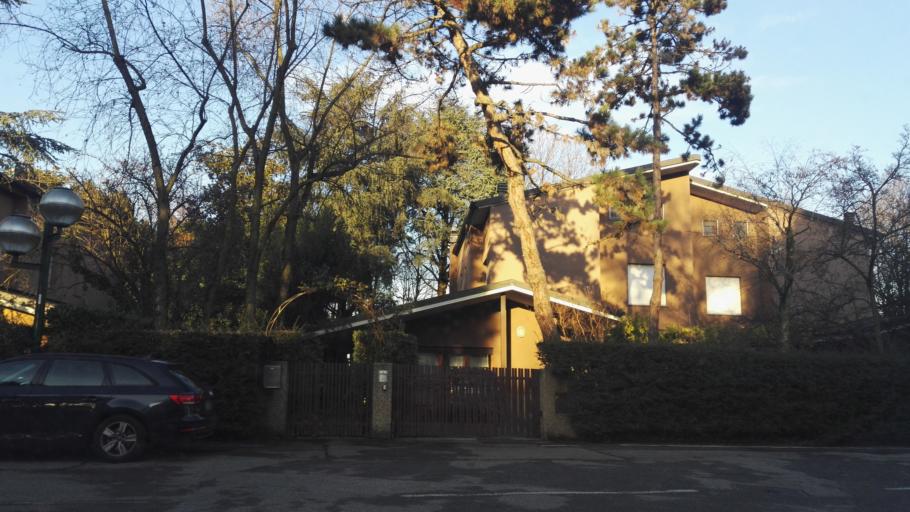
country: IT
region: Lombardy
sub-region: Citta metropolitana di Milano
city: San Bovio-San Felice
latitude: 45.4758
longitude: 9.3125
